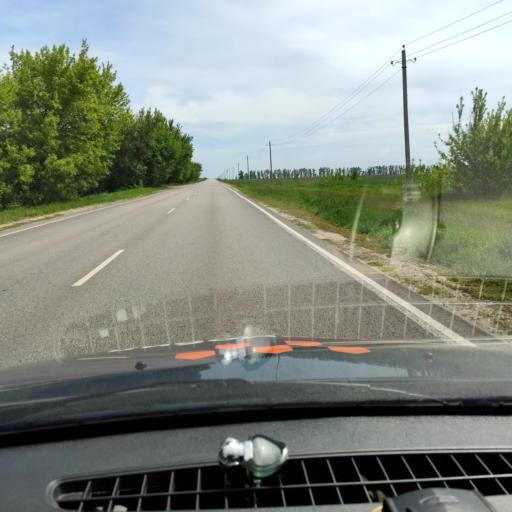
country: RU
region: Voronezj
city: Novaya Usman'
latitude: 51.5728
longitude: 39.3753
